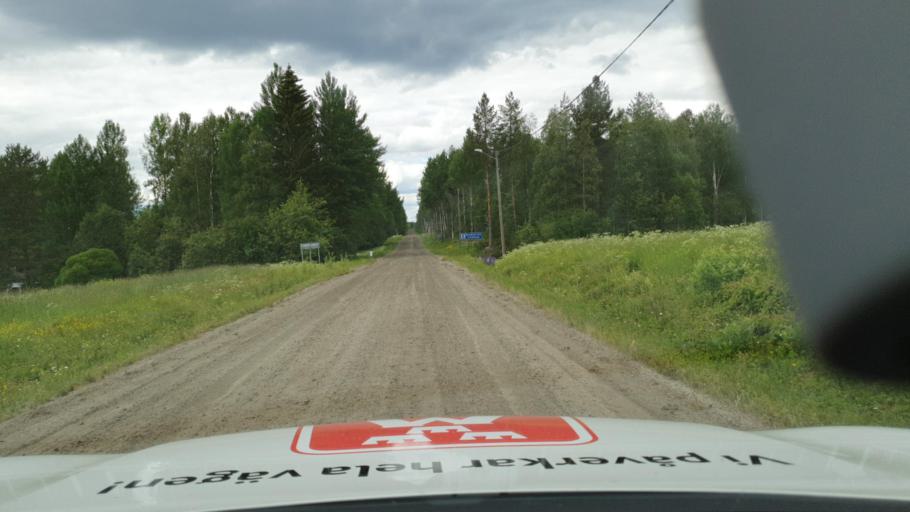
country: SE
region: Vaesterbotten
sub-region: Bjurholms Kommun
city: Bjurholm
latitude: 63.8217
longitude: 19.0219
